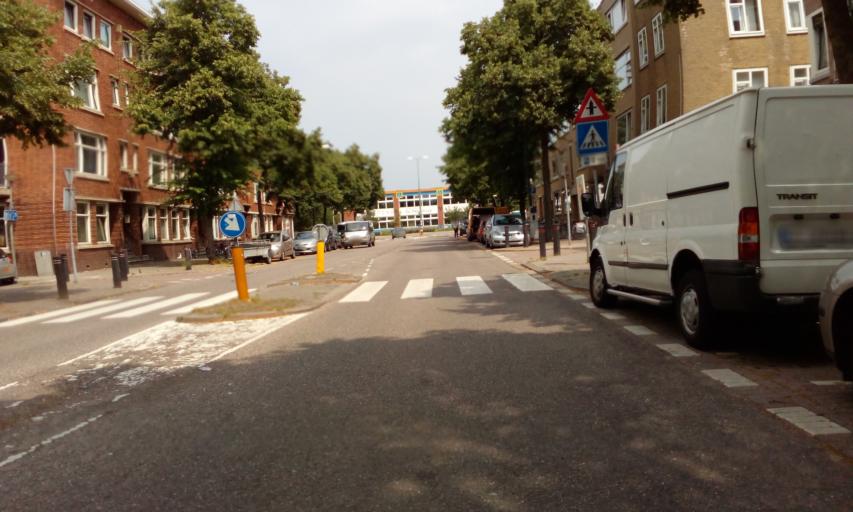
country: NL
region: South Holland
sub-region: Gemeente Schiedam
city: Schiedam
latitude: 51.9176
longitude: 4.4120
